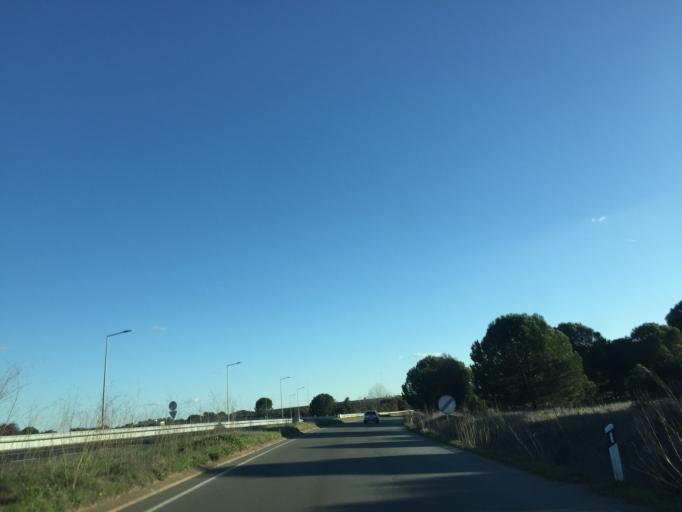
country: PT
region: Setubal
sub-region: Grandola
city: Grandola
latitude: 38.1157
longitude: -8.4187
